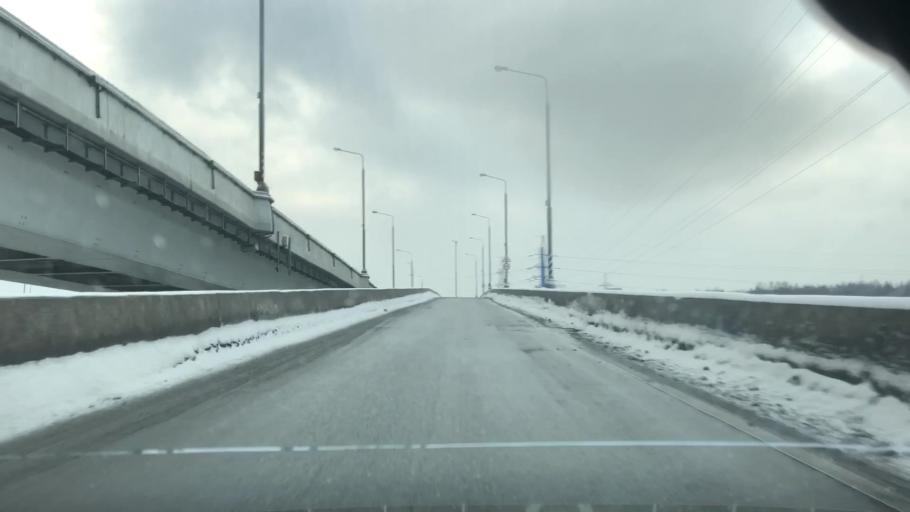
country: RU
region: Moskovskaya
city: Bol'shaya Setun'
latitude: 55.7019
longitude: 37.4200
